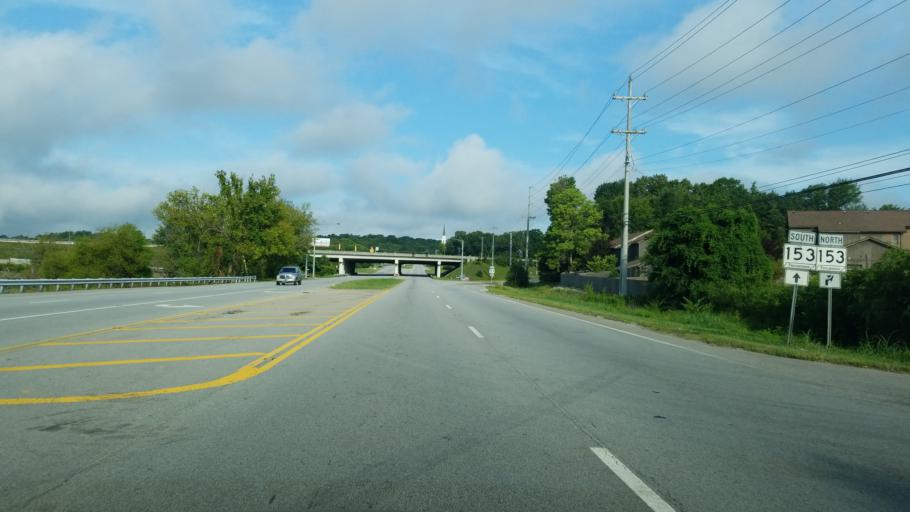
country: US
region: Tennessee
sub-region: Hamilton County
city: East Chattanooga
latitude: 35.0747
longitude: -85.1962
